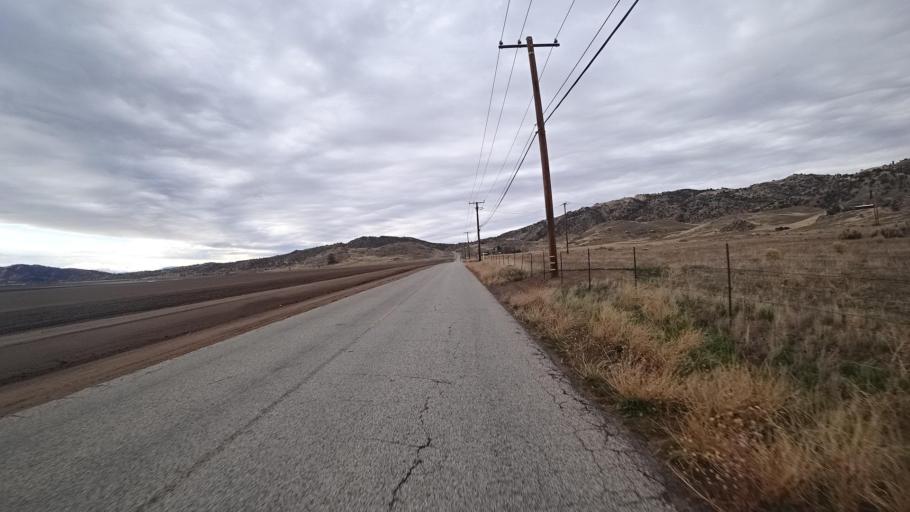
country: US
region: California
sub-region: Kern County
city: Bear Valley Springs
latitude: 35.1234
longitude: -118.6041
